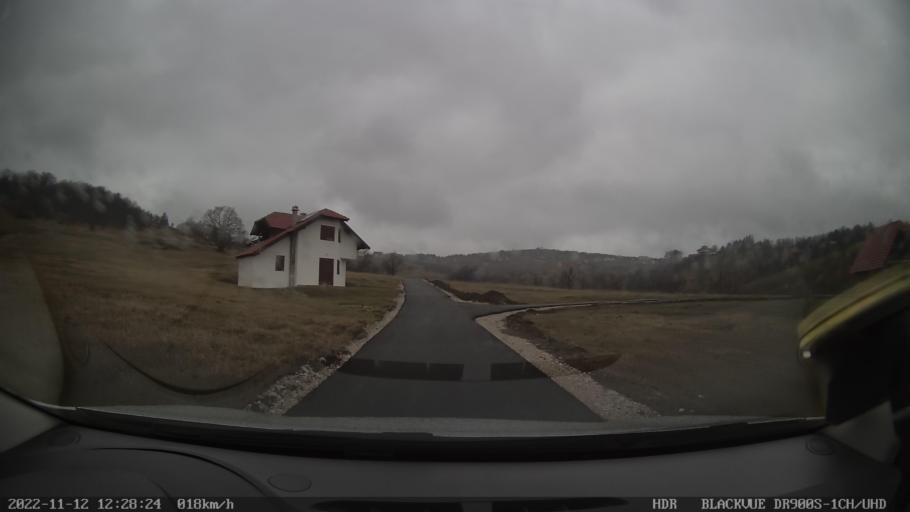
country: RS
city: Zlatibor
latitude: 43.7040
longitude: 19.7189
